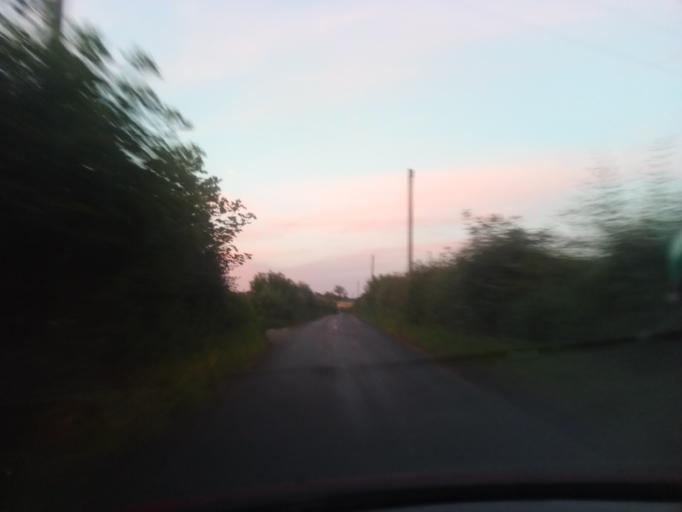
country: GB
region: England
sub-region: Northumberland
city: Wall
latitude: 55.0004
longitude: -2.1959
